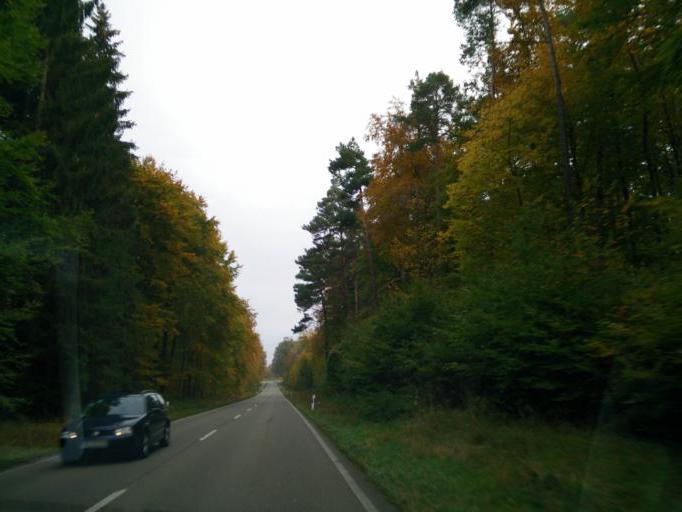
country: DE
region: Baden-Wuerttemberg
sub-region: Tuebingen Region
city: Dettenhausen
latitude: 48.5879
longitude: 9.1063
